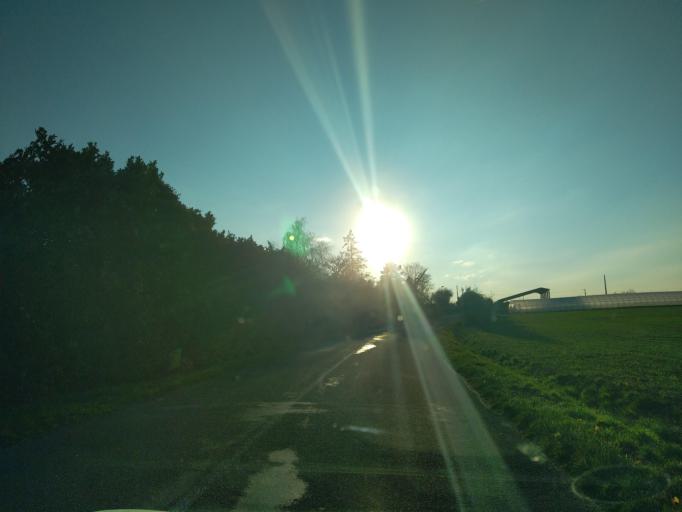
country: FR
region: Pays de la Loire
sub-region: Departement de la Vendee
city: Maillezais
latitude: 46.3393
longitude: -0.7726
